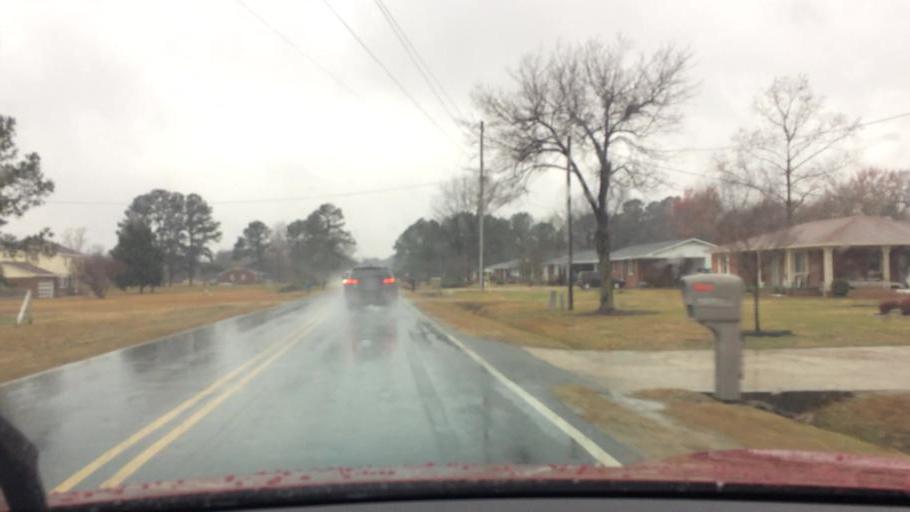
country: US
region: North Carolina
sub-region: Wayne County
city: Goldsboro
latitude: 35.4125
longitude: -77.9285
